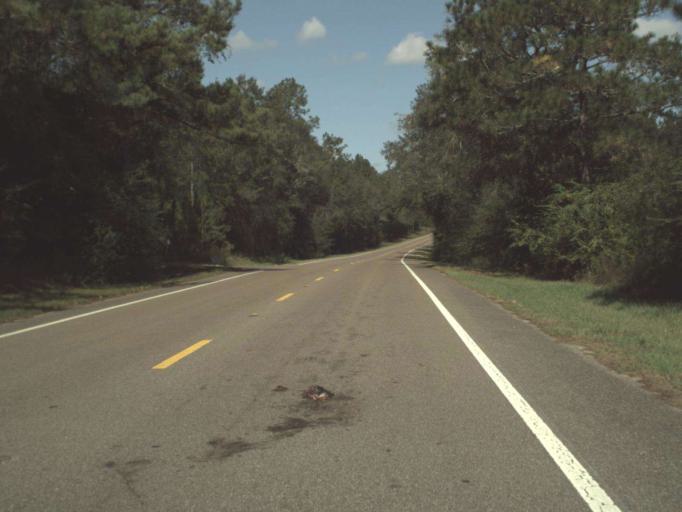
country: US
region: Florida
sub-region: Walton County
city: DeFuniak Springs
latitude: 30.8720
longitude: -86.1208
